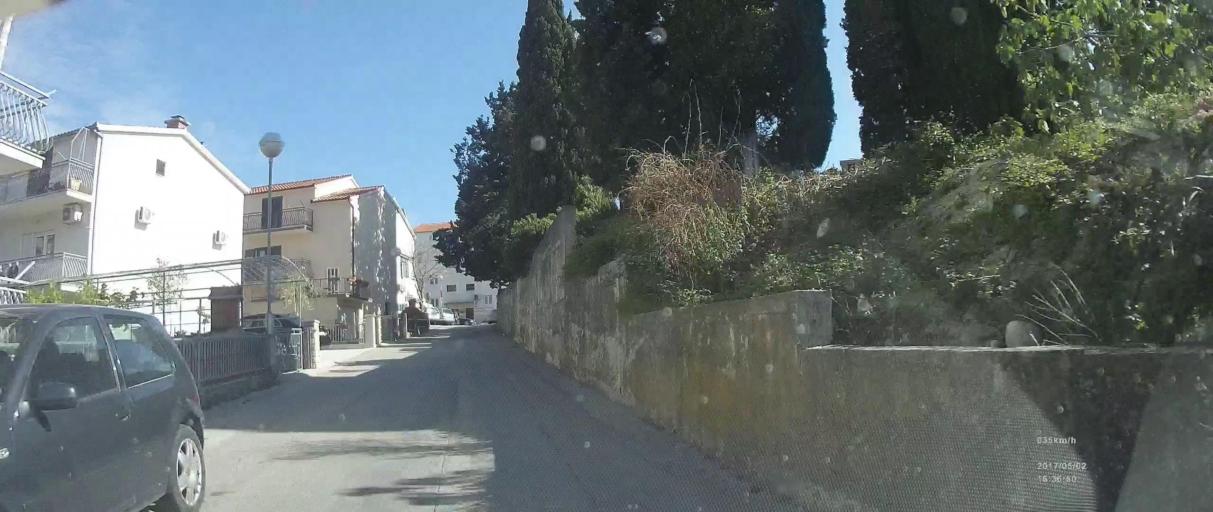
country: HR
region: Splitsko-Dalmatinska
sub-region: Grad Split
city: Stobrec
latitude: 43.5039
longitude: 16.5210
